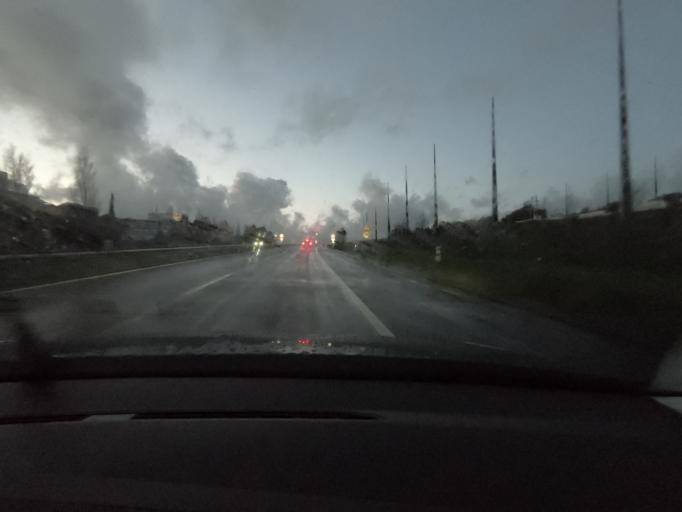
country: PT
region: Lisbon
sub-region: Sintra
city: Cacem
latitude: 38.7452
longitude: -9.3027
